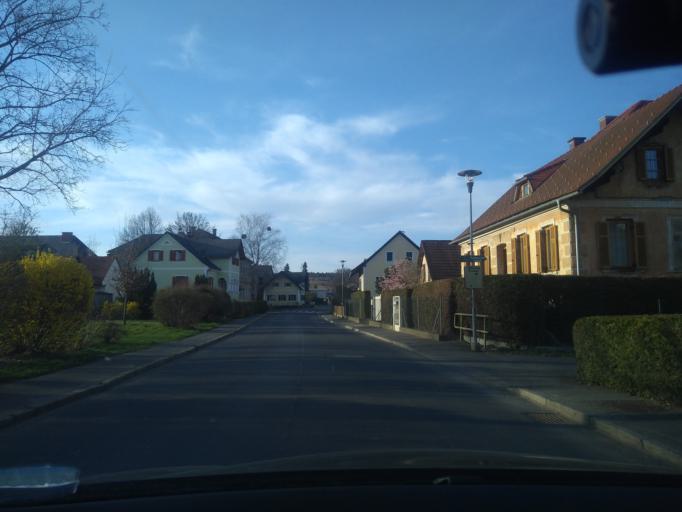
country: AT
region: Styria
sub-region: Politischer Bezirk Suedoststeiermark
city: Sankt Peter am Ottersbach
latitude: 46.8000
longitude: 15.7593
